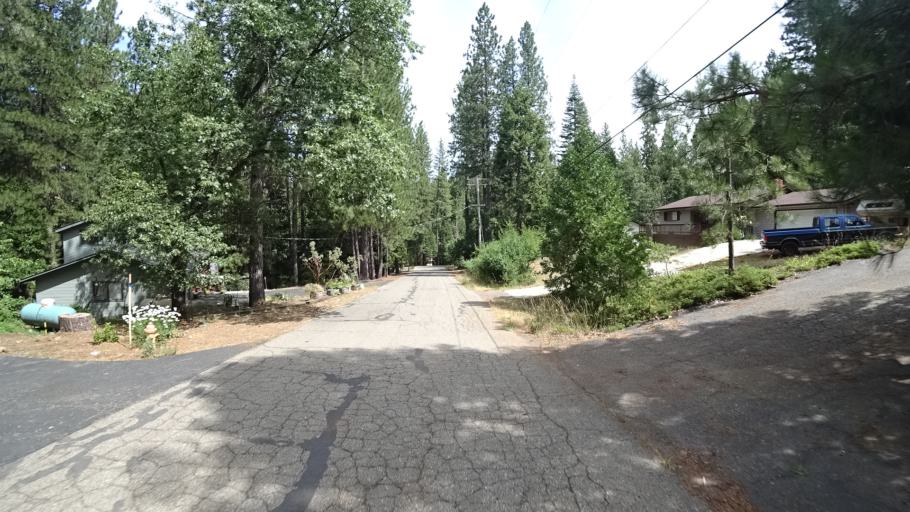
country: US
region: California
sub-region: Calaveras County
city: Arnold
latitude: 38.2450
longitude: -120.3546
